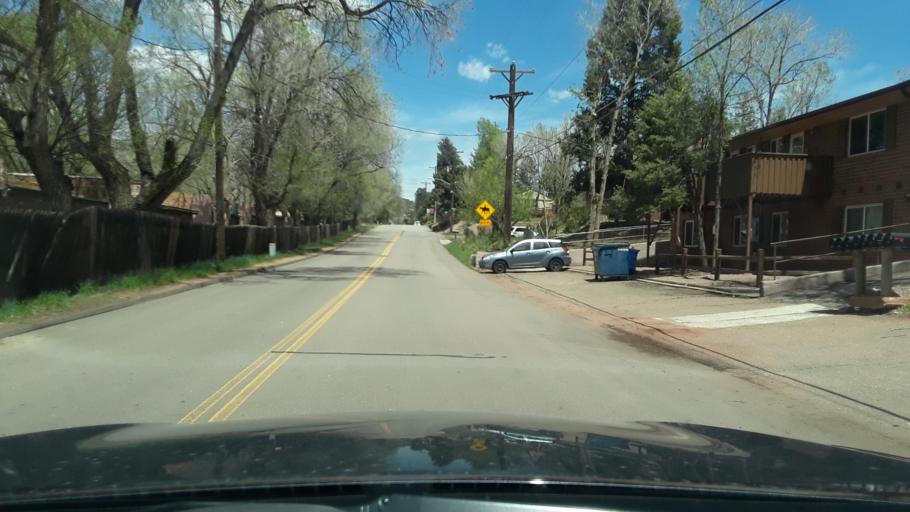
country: US
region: Colorado
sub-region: El Paso County
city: Manitou Springs
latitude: 38.8596
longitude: -104.8847
